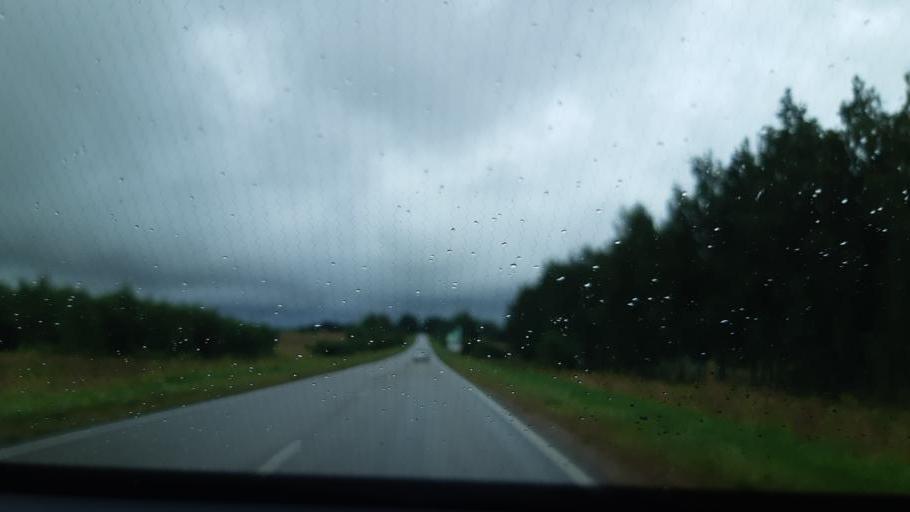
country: RU
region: Smolensk
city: Gagarin
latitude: 55.6285
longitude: 34.9623
